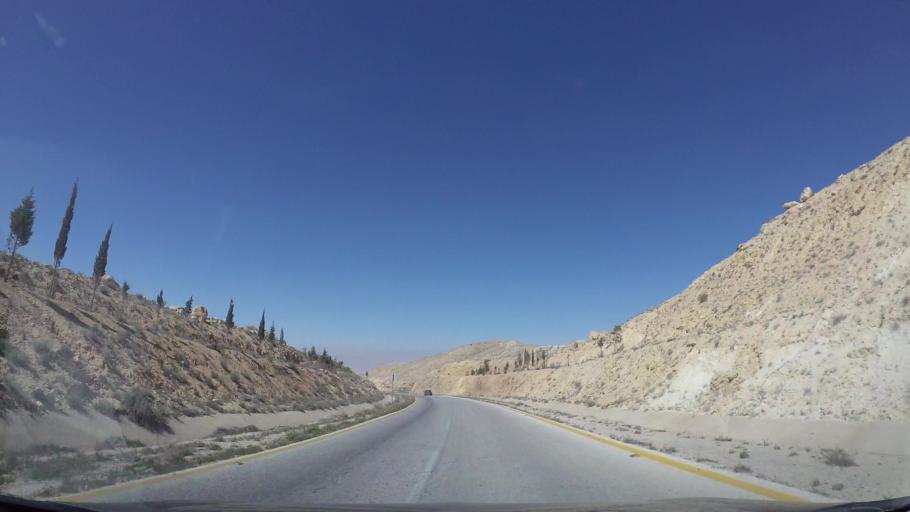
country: JO
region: Tafielah
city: At Tafilah
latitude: 30.8532
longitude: 35.5539
